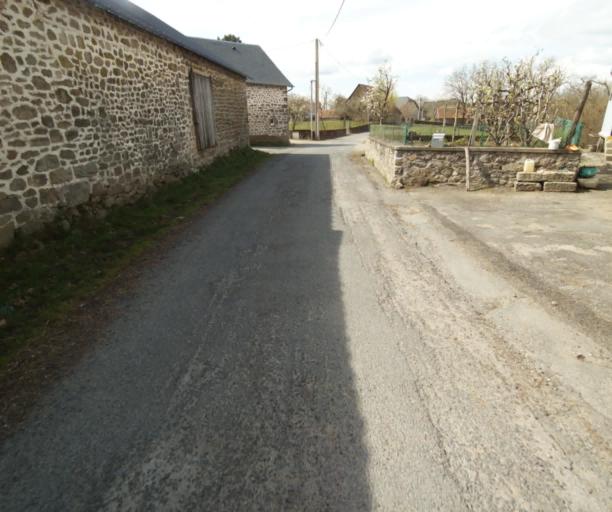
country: FR
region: Limousin
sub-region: Departement de la Correze
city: Correze
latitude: 45.3675
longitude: 1.8953
